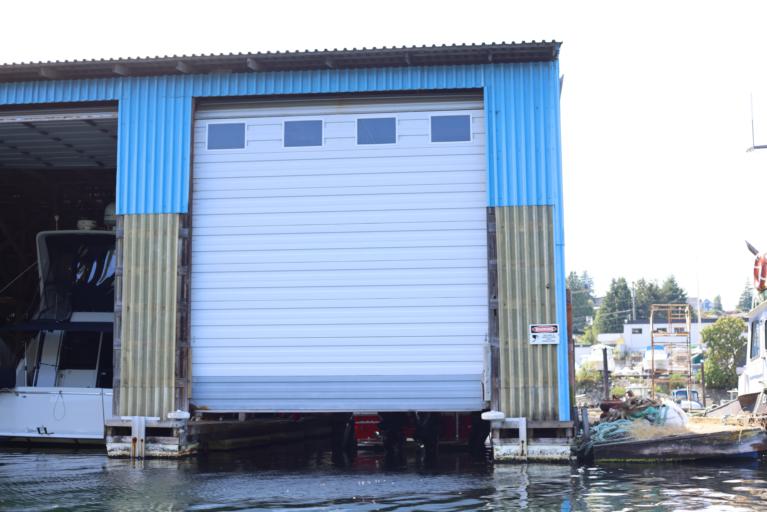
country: CA
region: British Columbia
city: Nanaimo
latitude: 49.1868
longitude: -123.9456
